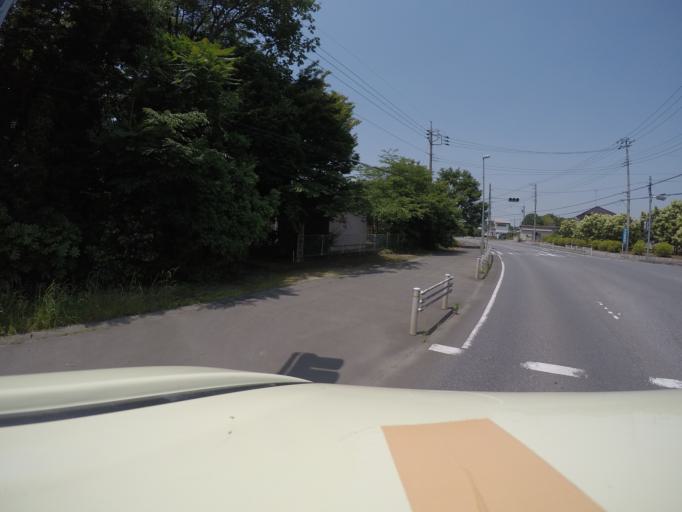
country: JP
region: Ibaraki
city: Iwai
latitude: 36.0392
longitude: 139.9341
